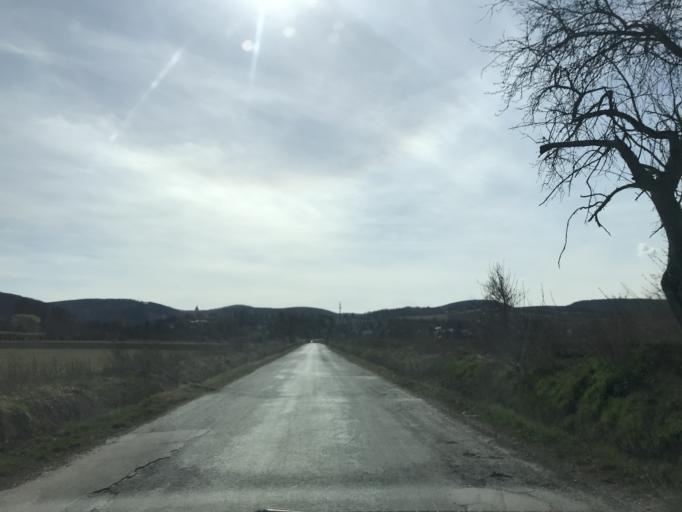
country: HU
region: Komarom-Esztergom
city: Pilismarot
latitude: 47.7918
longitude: 18.8794
